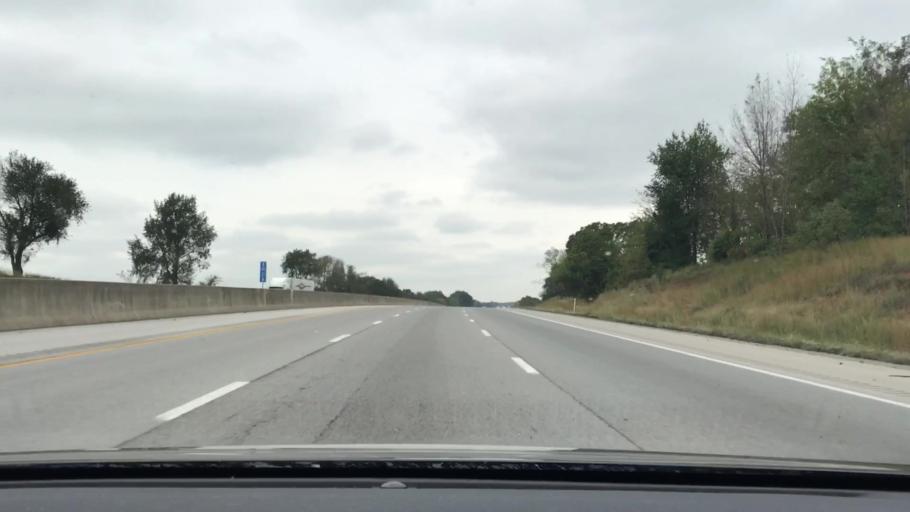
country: US
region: Kentucky
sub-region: Warren County
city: Plano
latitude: 36.7866
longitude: -86.4760
